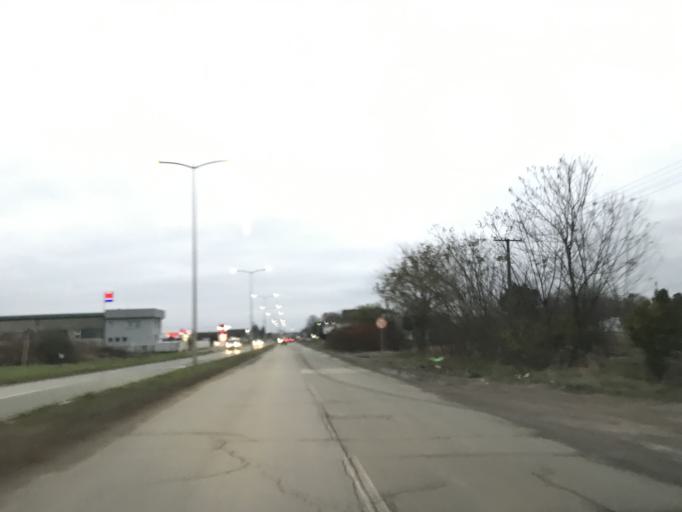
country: RS
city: Veternik
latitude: 45.2799
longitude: 19.7876
